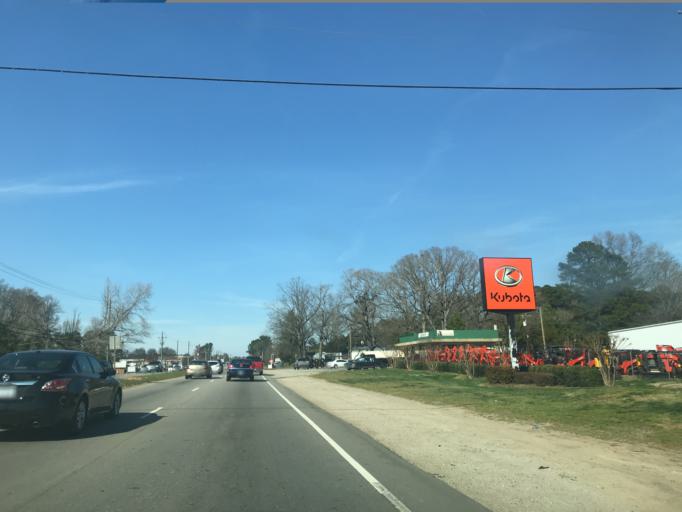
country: US
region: North Carolina
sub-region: Wake County
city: Garner
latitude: 35.7134
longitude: -78.6570
